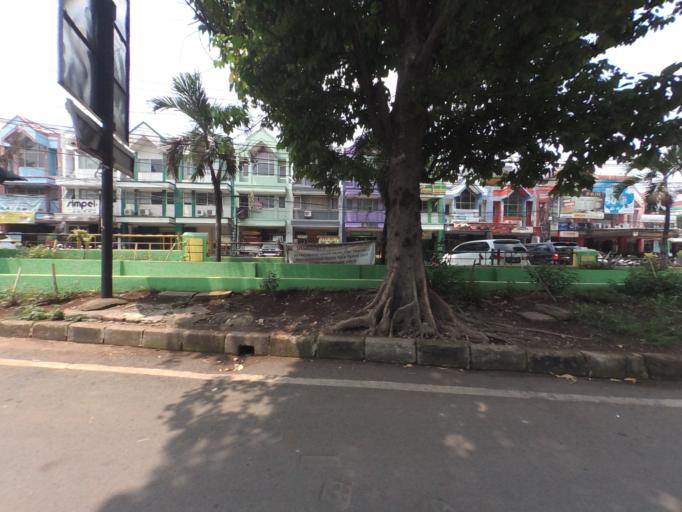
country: ID
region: West Java
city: Bogor
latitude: -6.5611
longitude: 106.7674
